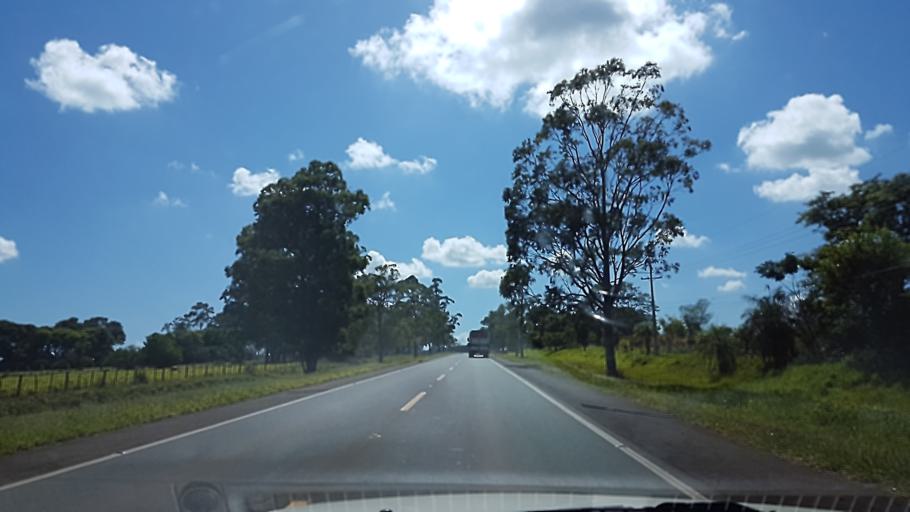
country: PY
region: Itapua
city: Carmen del Parana
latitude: -27.2212
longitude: -56.1126
